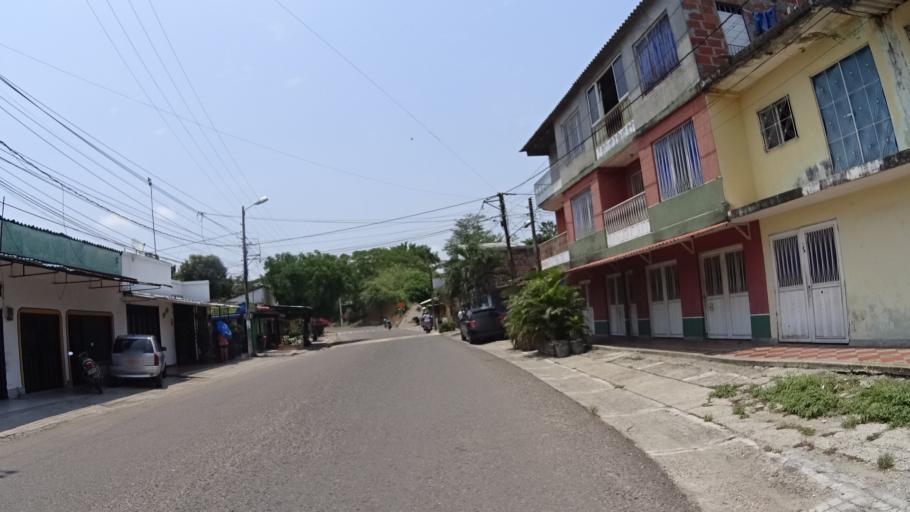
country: CO
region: Cundinamarca
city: Puerto Salgar
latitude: 5.4658
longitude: -74.6650
